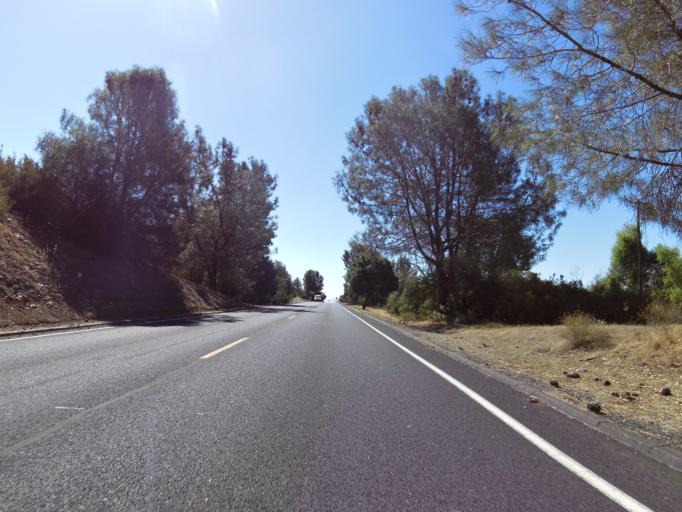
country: US
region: California
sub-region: Tuolumne County
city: Tuolumne City
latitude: 37.7128
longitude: -120.3177
